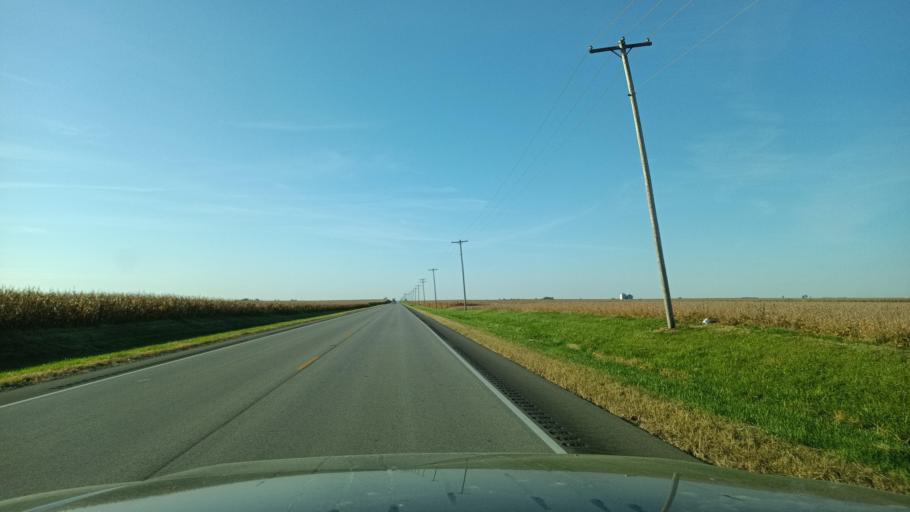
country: US
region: Illinois
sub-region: Douglas County
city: Villa Grove
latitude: 39.7848
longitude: -87.9397
